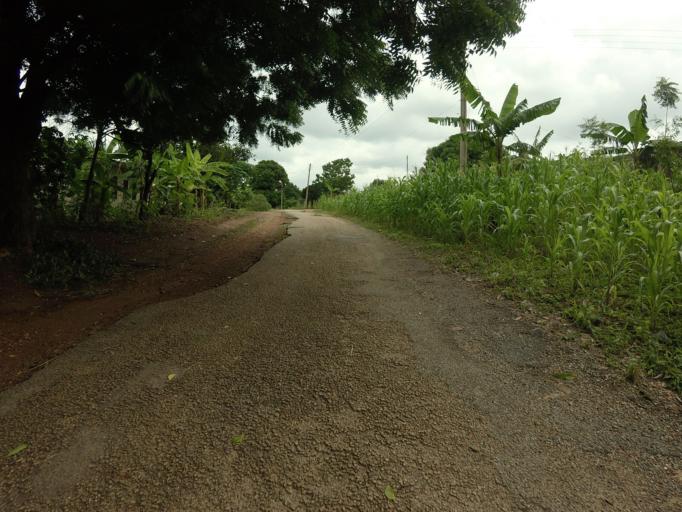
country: GH
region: Volta
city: Ho
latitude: 6.6033
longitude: 0.4599
